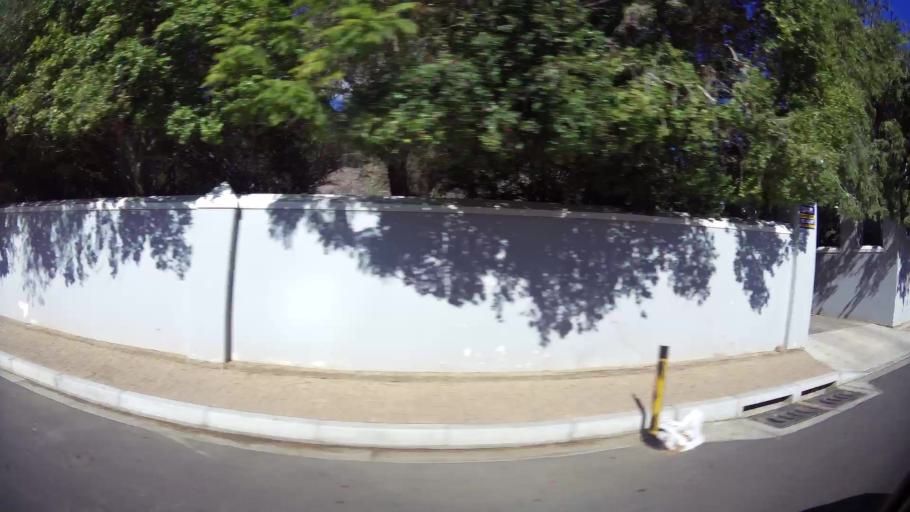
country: ZA
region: Western Cape
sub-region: Cape Winelands District Municipality
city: Ashton
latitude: -33.7905
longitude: 20.1139
